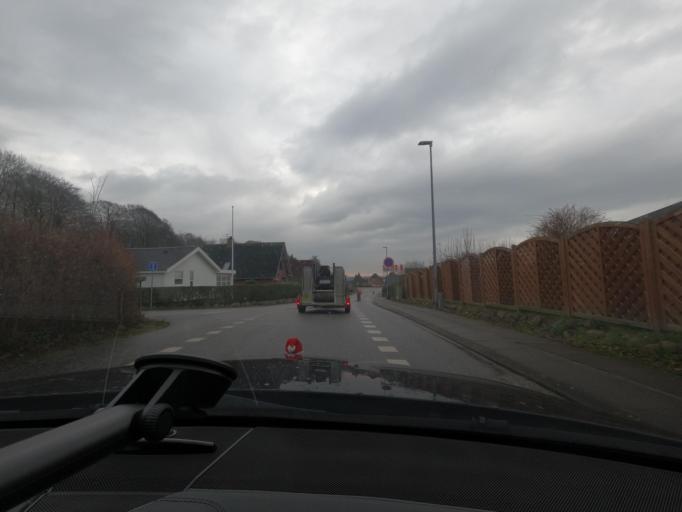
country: DK
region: South Denmark
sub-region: Sonderborg Kommune
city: Horuphav
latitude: 54.9120
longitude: 9.8940
